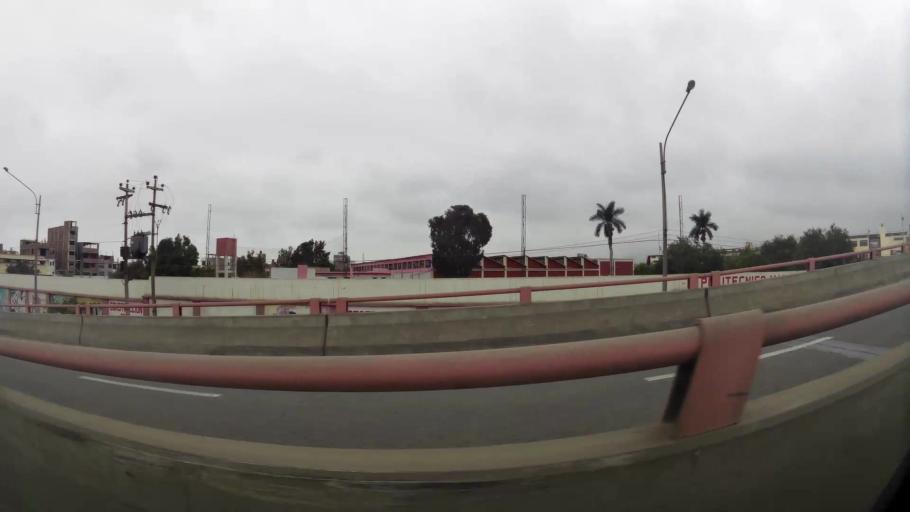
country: PE
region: La Libertad
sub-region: Provincia de Trujillo
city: Trujillo
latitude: -8.1247
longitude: -79.0247
